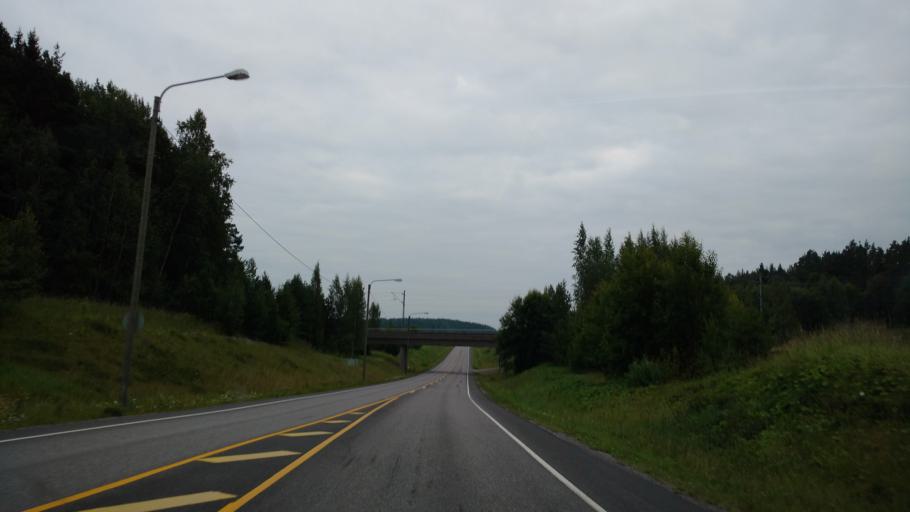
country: FI
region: Varsinais-Suomi
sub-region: Salo
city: Halikko
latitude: 60.3978
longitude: 23.0527
